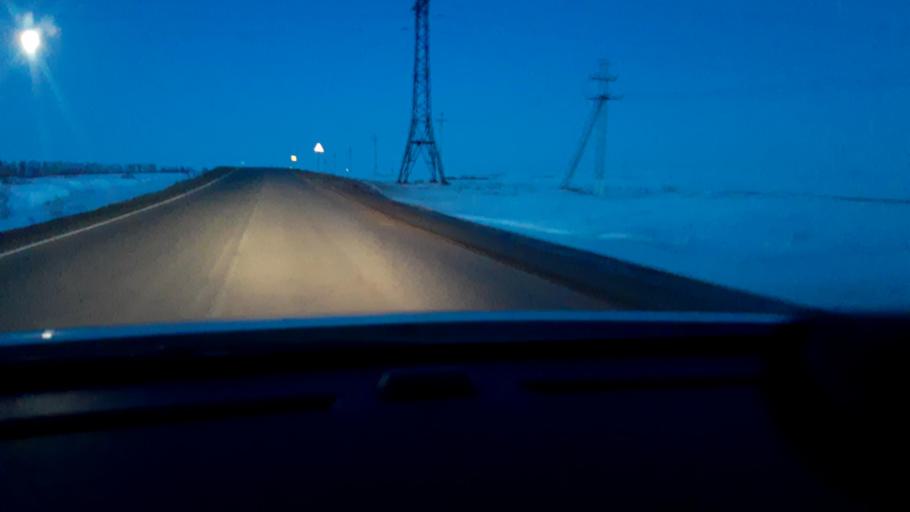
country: RU
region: Bashkortostan
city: Avdon
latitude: 54.3834
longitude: 55.7999
